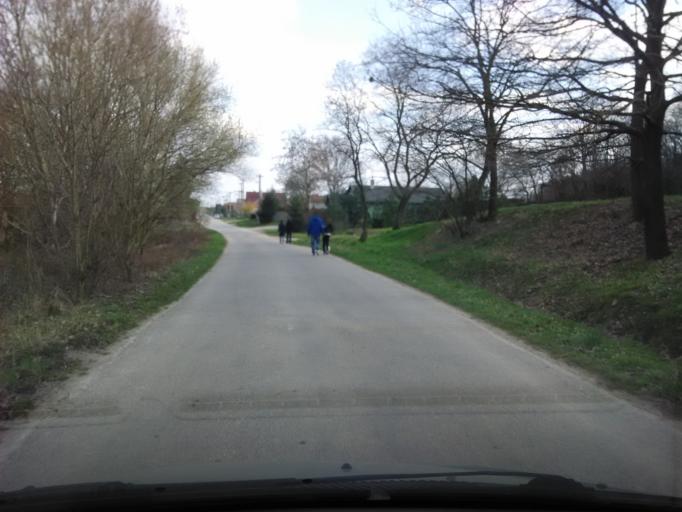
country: SK
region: Nitriansky
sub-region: Okres Nitra
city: Nitra
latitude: 48.3872
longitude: 18.2144
